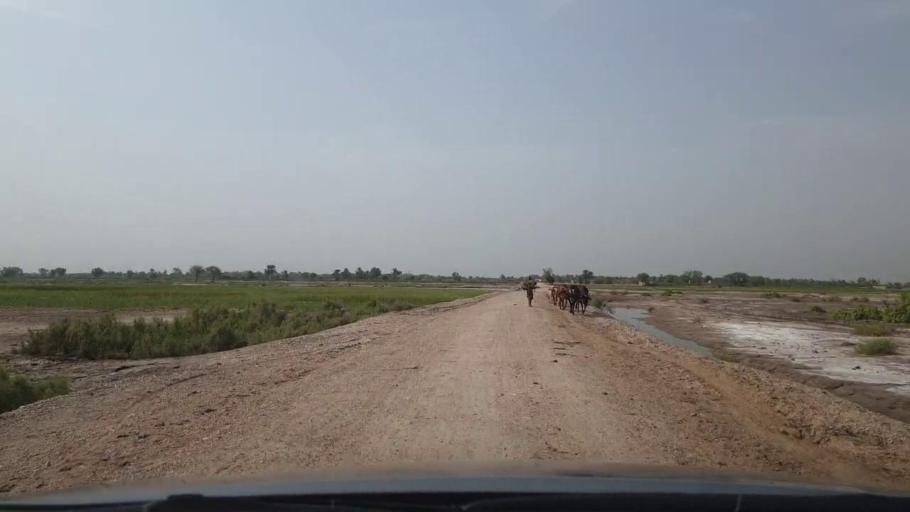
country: PK
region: Sindh
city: Rohri
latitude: 27.6687
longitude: 69.0137
